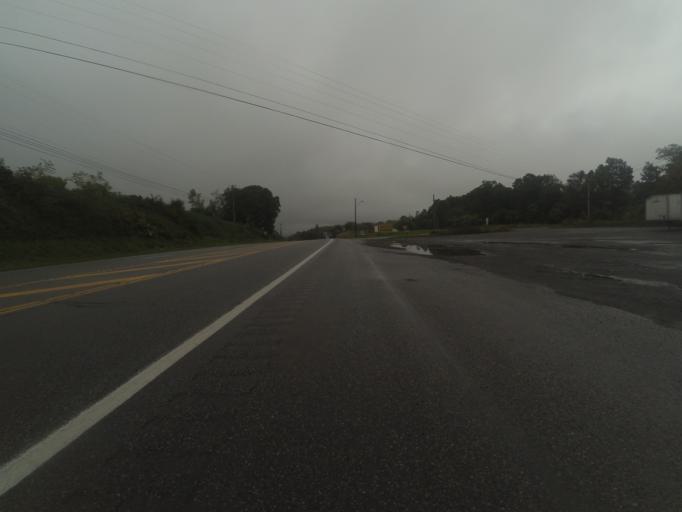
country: US
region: Pennsylvania
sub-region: Huntingdon County
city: McConnellstown
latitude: 40.5037
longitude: -78.0673
